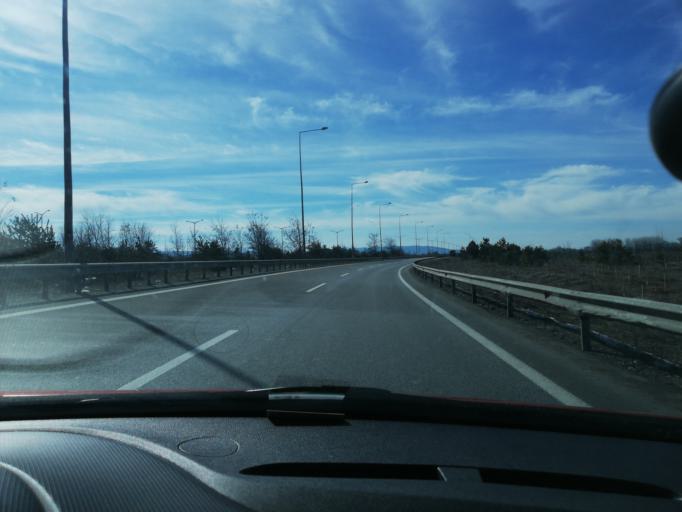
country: TR
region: Bolu
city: Gerede
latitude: 40.7394
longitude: 32.1912
